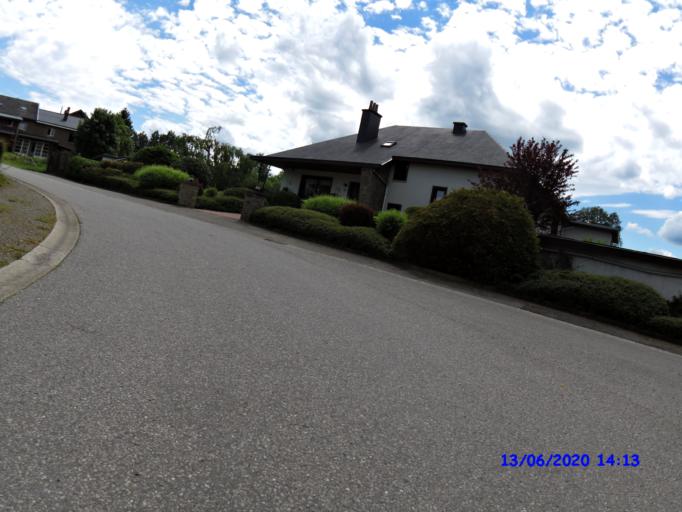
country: BE
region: Wallonia
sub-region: Province de Liege
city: Stavelot
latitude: 50.4100
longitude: 5.9688
